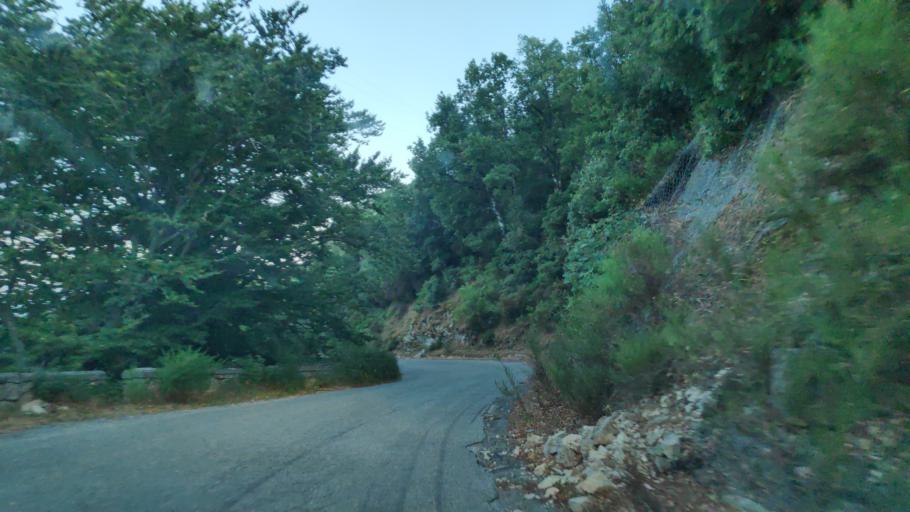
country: IT
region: Calabria
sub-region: Provincia di Vibo-Valentia
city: Nardodipace
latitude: 38.4813
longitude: 16.3810
